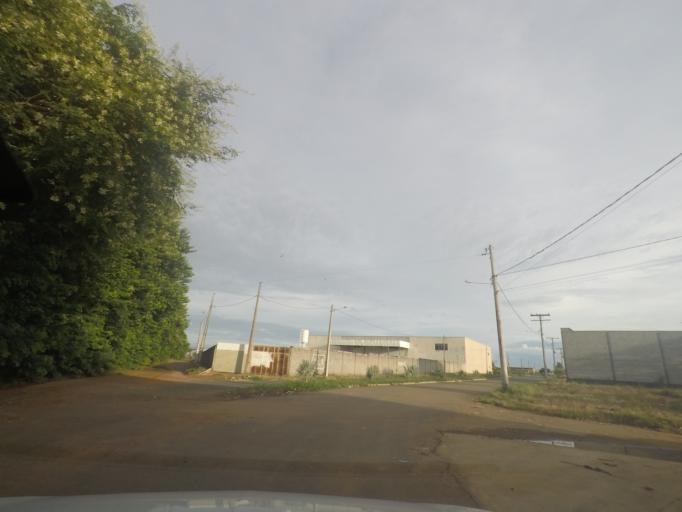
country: BR
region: Goias
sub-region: Trindade
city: Trindade
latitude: -16.7273
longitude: -49.4393
